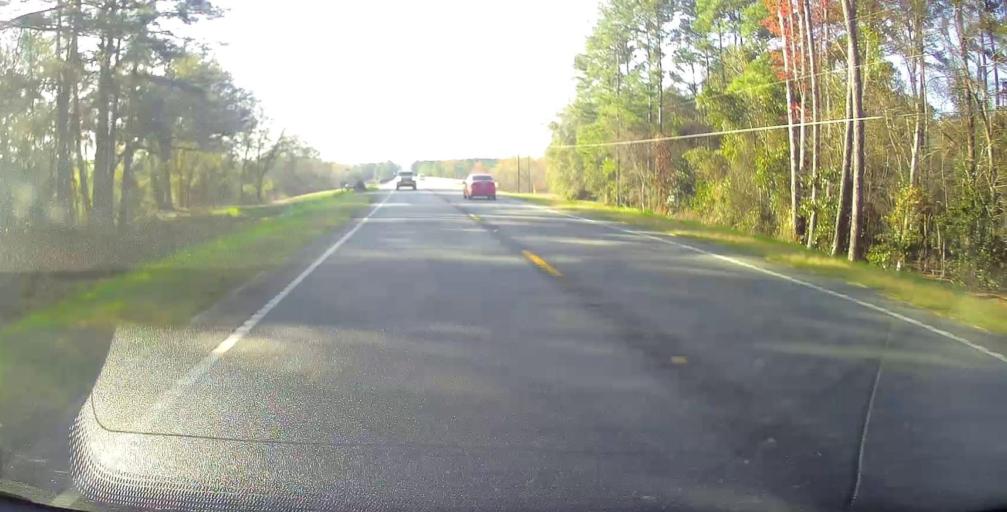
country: US
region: Georgia
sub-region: Tattnall County
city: Reidsville
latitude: 32.1165
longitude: -82.1874
